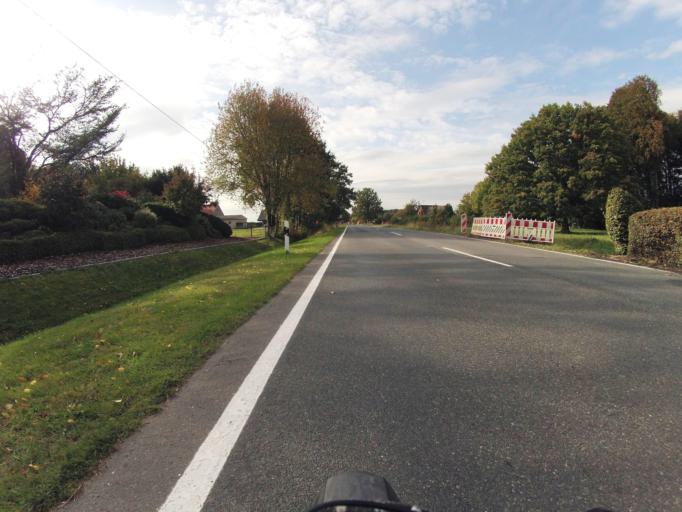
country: DE
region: North Rhine-Westphalia
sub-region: Regierungsbezirk Munster
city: Mettingen
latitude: 52.2811
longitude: 7.7973
